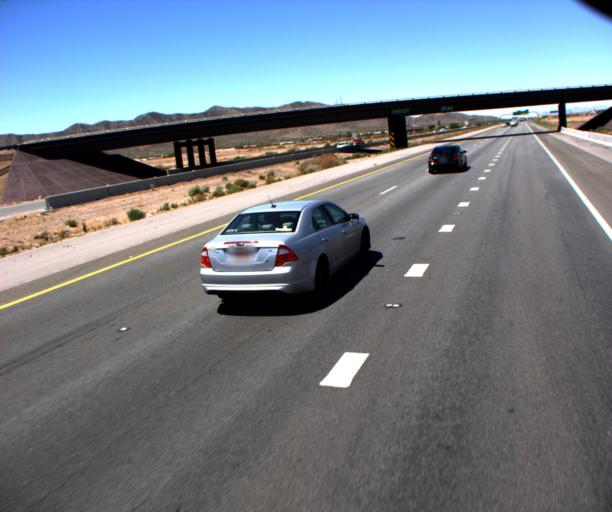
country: US
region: Arizona
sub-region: Pinal County
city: Arizona City
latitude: 32.8089
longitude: -111.6700
